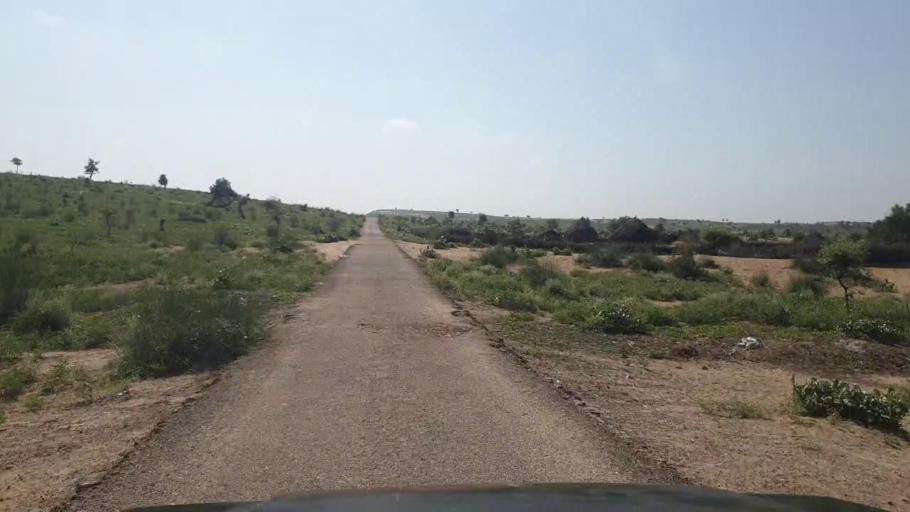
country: PK
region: Sindh
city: Islamkot
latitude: 25.1685
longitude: 70.4010
